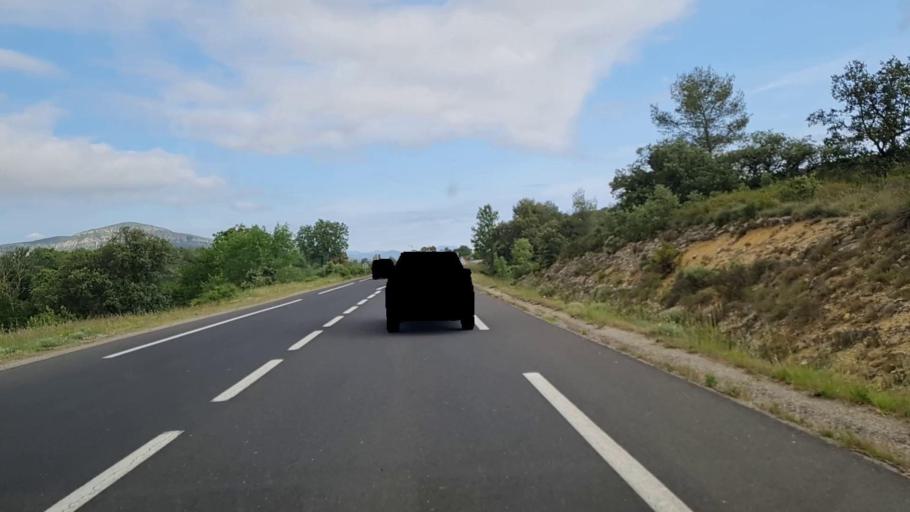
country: FR
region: Languedoc-Roussillon
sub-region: Departement du Gard
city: Quissac
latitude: 43.8903
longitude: 4.0131
